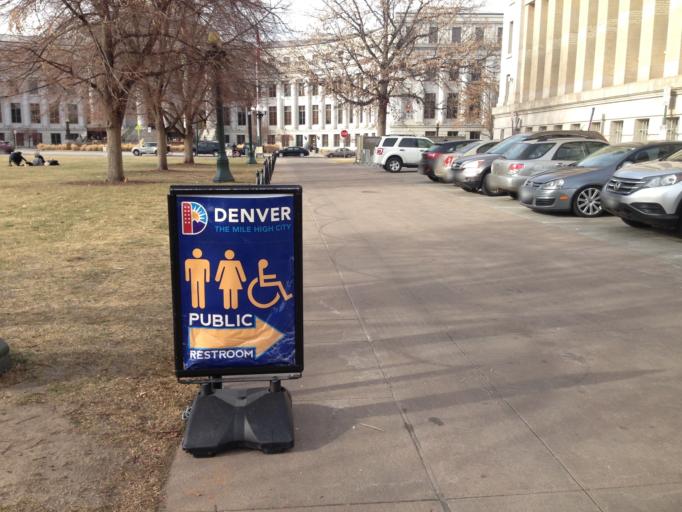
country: US
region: Colorado
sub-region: Denver County
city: Denver
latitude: 39.7395
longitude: -104.9894
